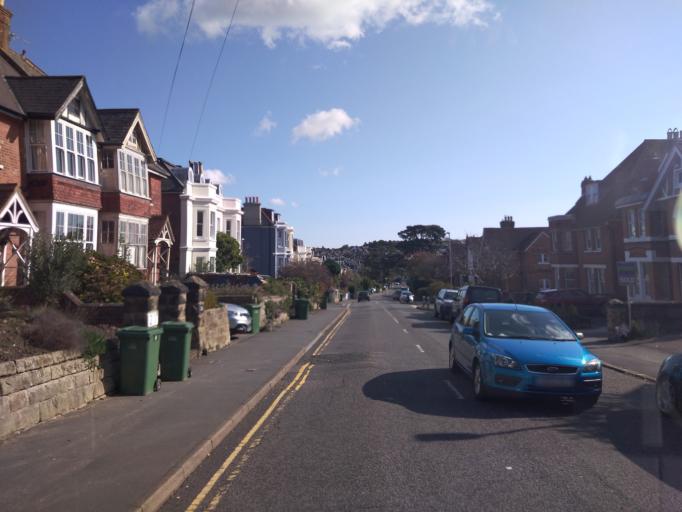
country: GB
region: England
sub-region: East Sussex
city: Saint Leonards-on-Sea
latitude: 50.8634
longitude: 0.5535
